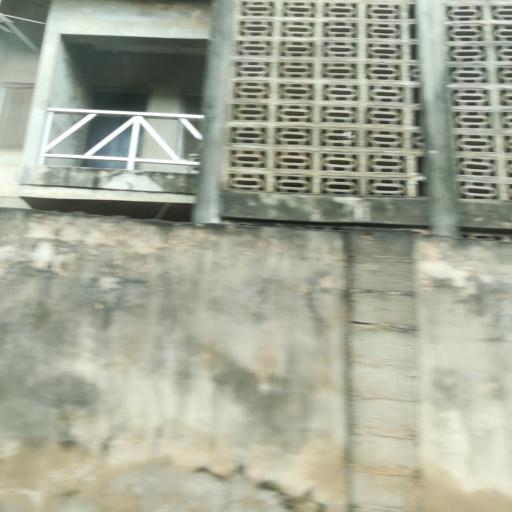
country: NG
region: Lagos
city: Agege
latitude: 6.5931
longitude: 3.2976
